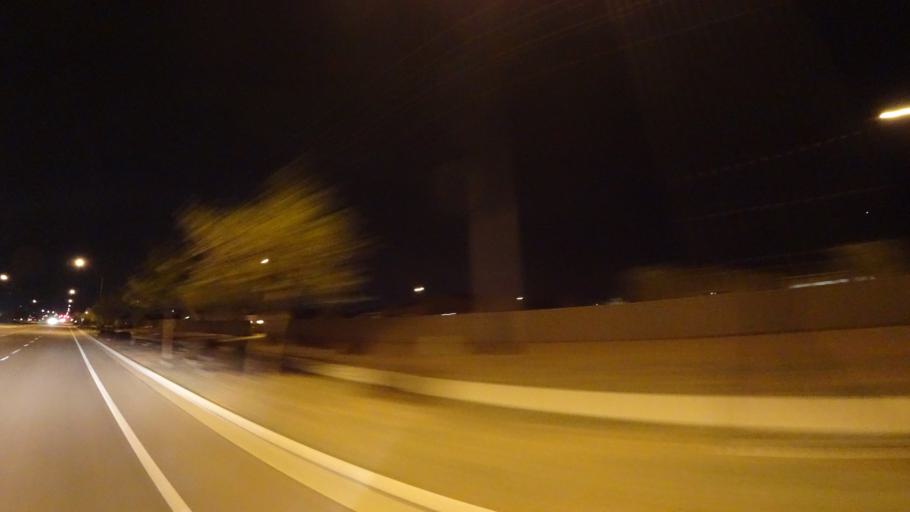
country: US
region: Arizona
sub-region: Maricopa County
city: Chandler
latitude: 33.2576
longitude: -111.7726
